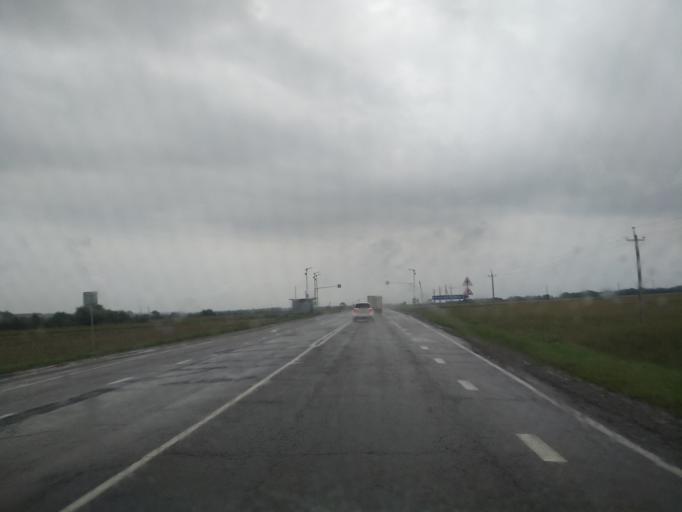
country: RU
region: Voronezj
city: Verkhnyaya Khava
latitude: 51.6780
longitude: 39.8730
